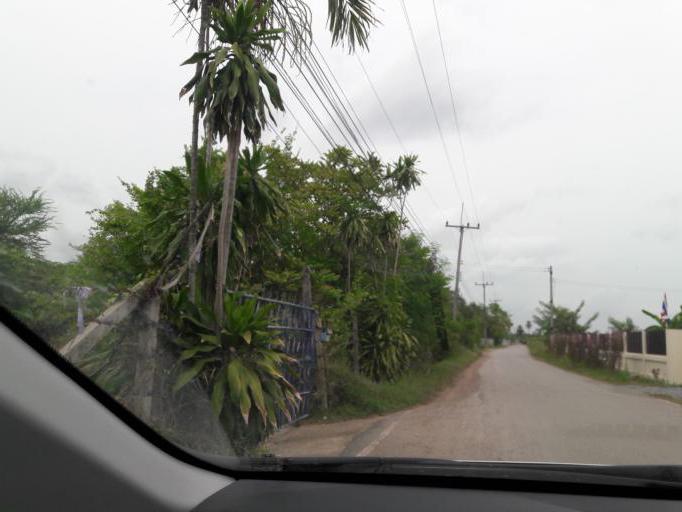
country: TH
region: Samut Sakhon
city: Ban Phaeo
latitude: 13.6244
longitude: 100.0268
